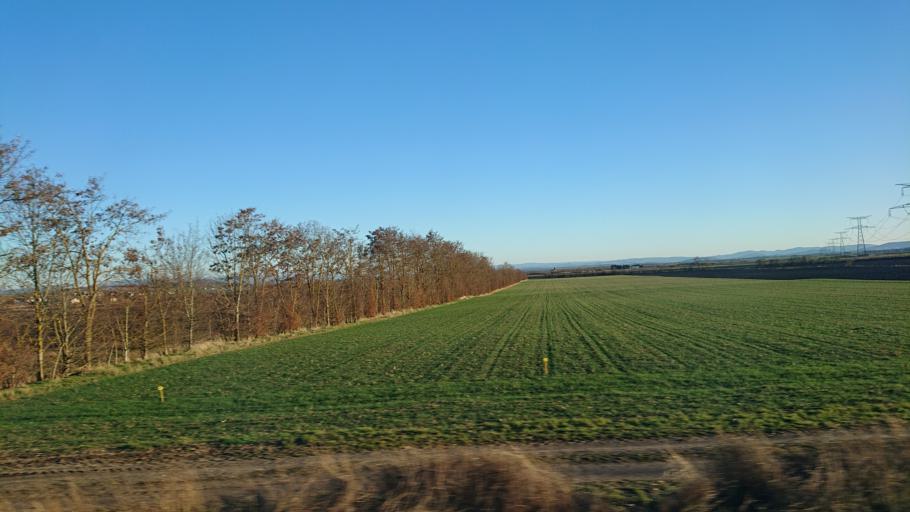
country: FR
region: Auvergne
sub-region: Departement du Puy-de-Dome
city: Maringues
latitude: 45.9752
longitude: 3.2777
